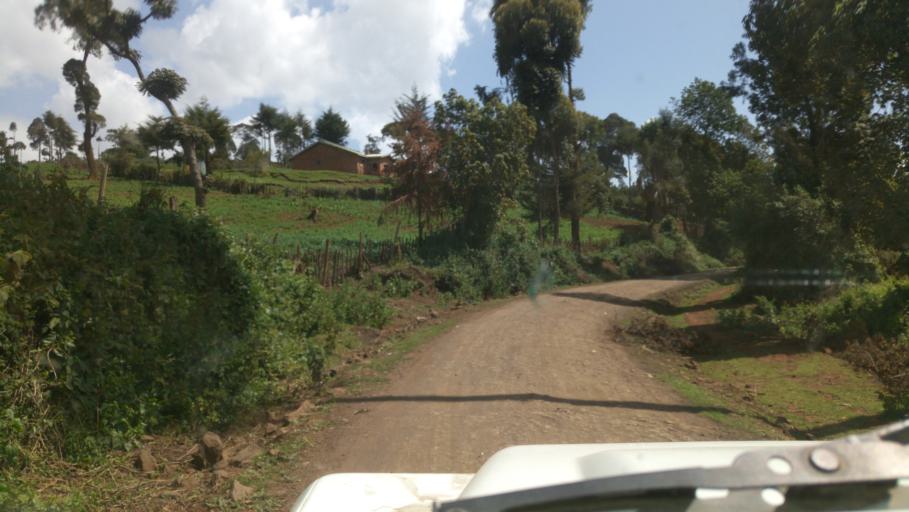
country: KE
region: Nakuru
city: Molo
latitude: -0.3285
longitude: 35.7016
